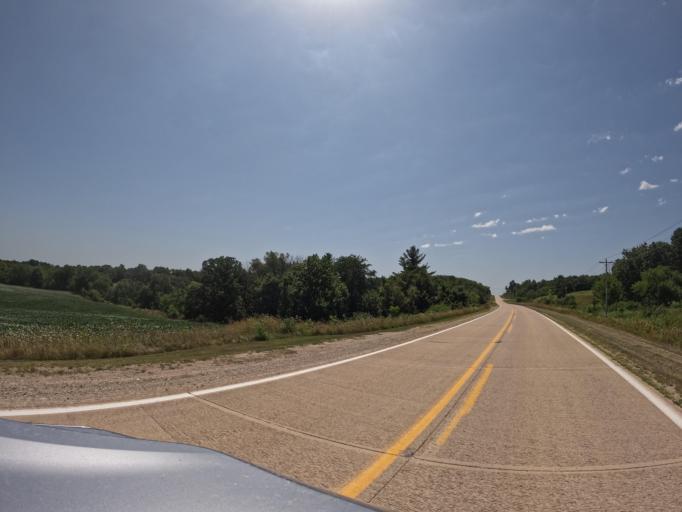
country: US
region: Iowa
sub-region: Henry County
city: Mount Pleasant
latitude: 40.9188
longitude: -91.5541
